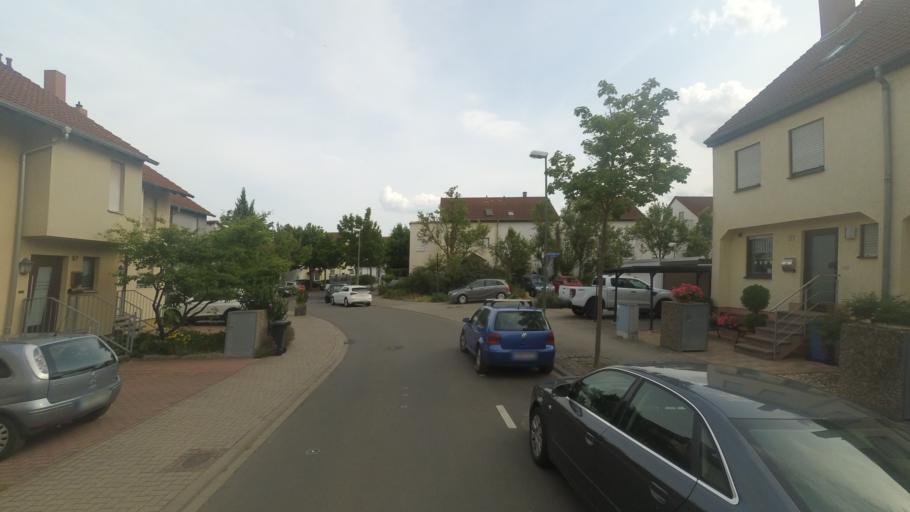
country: DE
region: Rheinland-Pfalz
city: Mutterstadt
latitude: 49.4696
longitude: 8.3324
